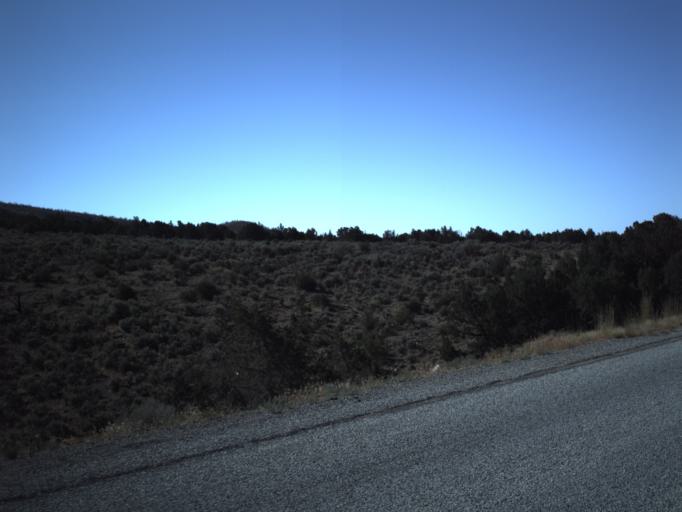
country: US
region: Utah
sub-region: Juab County
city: Mona
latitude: 39.7783
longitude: -112.1532
